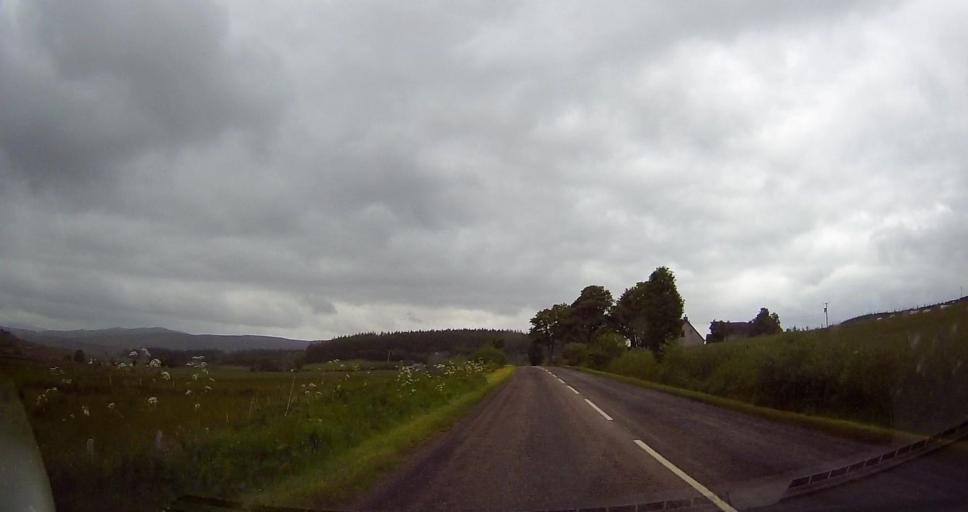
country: GB
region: Scotland
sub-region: Highland
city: Alness
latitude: 58.0187
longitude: -4.3648
